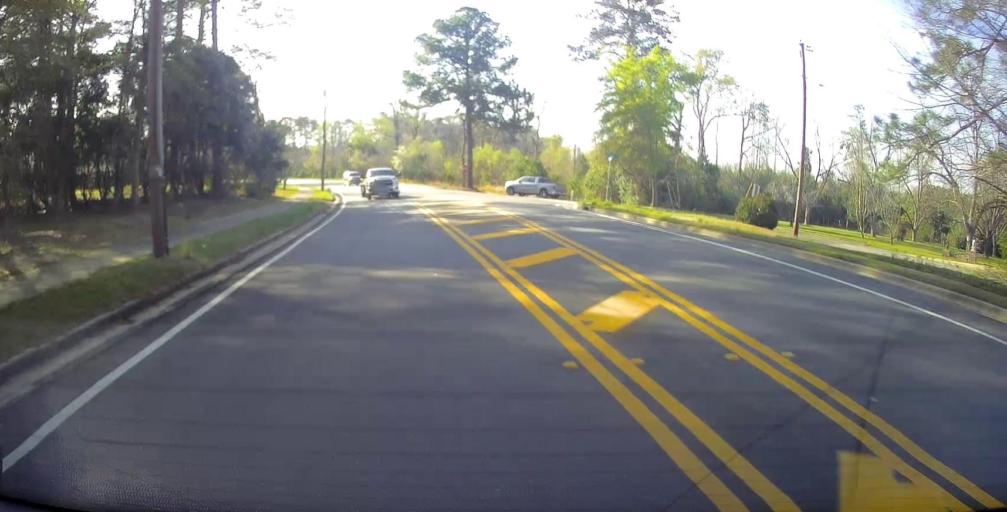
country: US
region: Georgia
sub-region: Montgomery County
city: Mount Vernon
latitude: 32.1866
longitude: -82.5729
